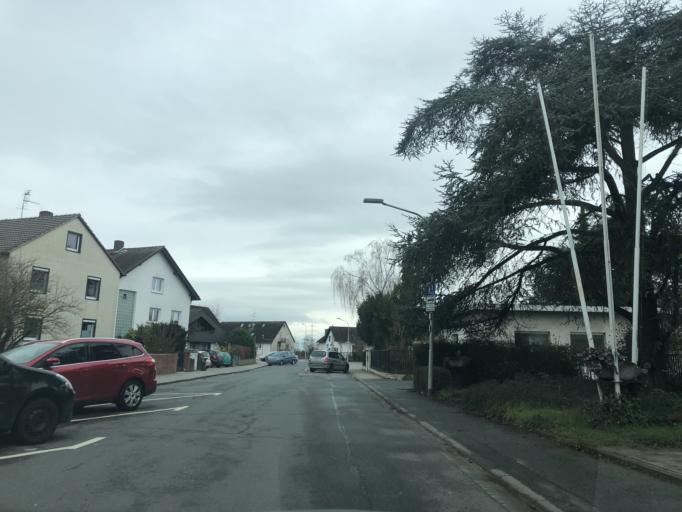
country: DE
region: Hesse
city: Pfungstadt
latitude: 49.8036
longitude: 8.5909
